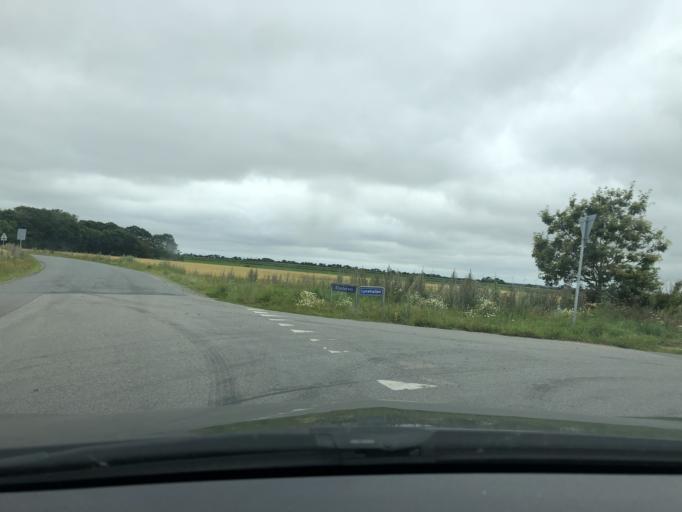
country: DK
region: Central Jutland
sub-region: Ringkobing-Skjern Kommune
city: Tarm
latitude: 55.8004
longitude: 8.4884
